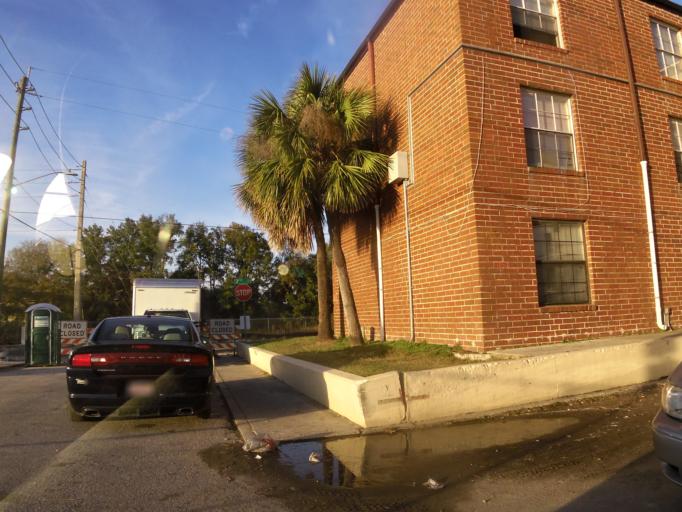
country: US
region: Florida
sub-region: Duval County
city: Jacksonville
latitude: 30.3435
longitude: -81.6389
